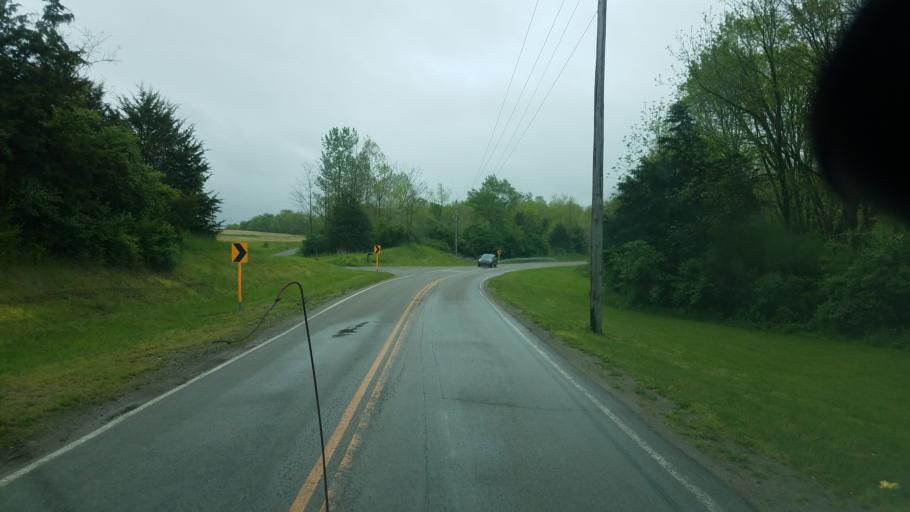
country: US
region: Ohio
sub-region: Highland County
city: Greenfield
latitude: 39.3359
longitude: -83.4669
